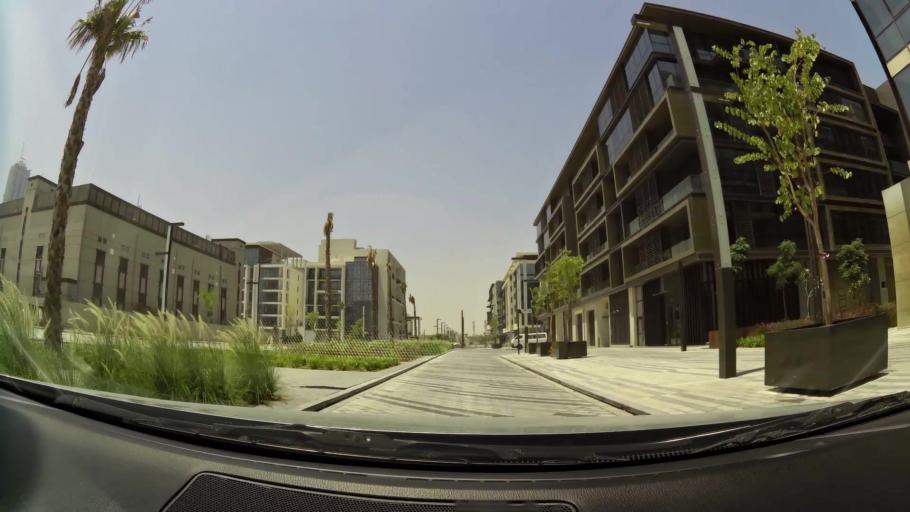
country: AE
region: Dubai
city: Dubai
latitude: 25.2035
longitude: 55.2636
